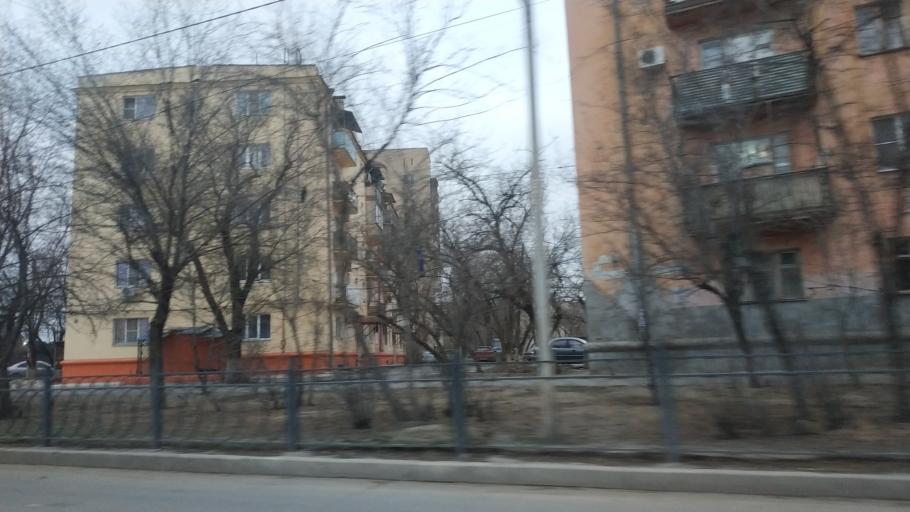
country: RU
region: Astrakhan
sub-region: Gorod Astrakhan'
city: Astrakhan'
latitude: 46.3335
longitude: 48.0138
